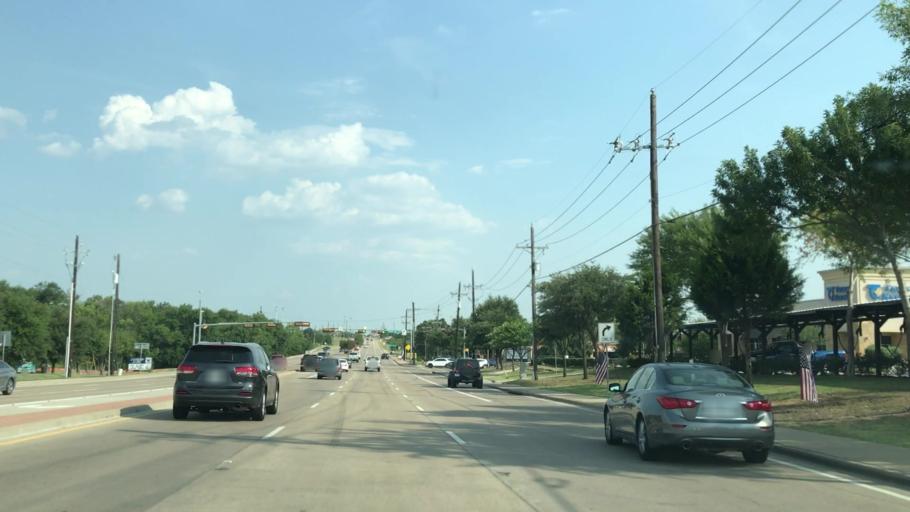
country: US
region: Texas
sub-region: Rockwall County
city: Rockwall
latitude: 32.9057
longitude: -96.4478
